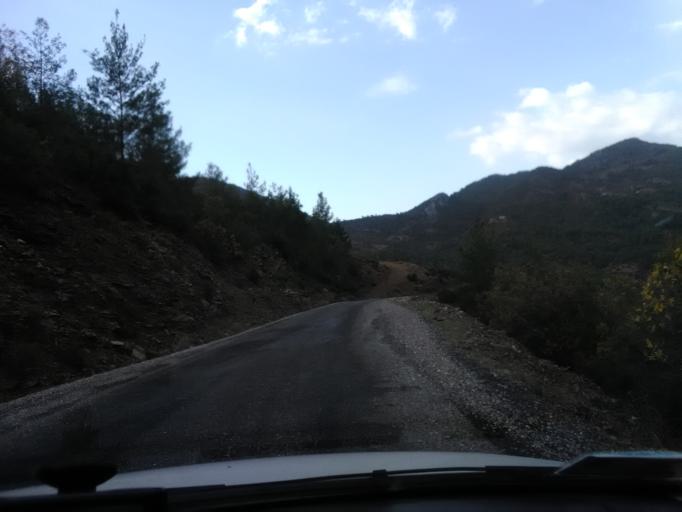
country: TR
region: Antalya
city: Gazipasa
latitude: 36.3030
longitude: 32.3847
